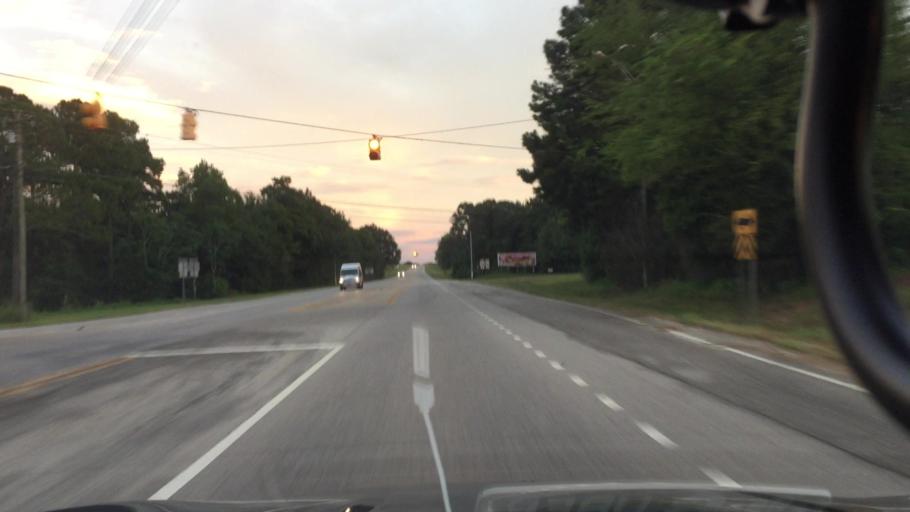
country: US
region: Alabama
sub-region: Coffee County
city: New Brockton
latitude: 31.4274
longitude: -85.8886
